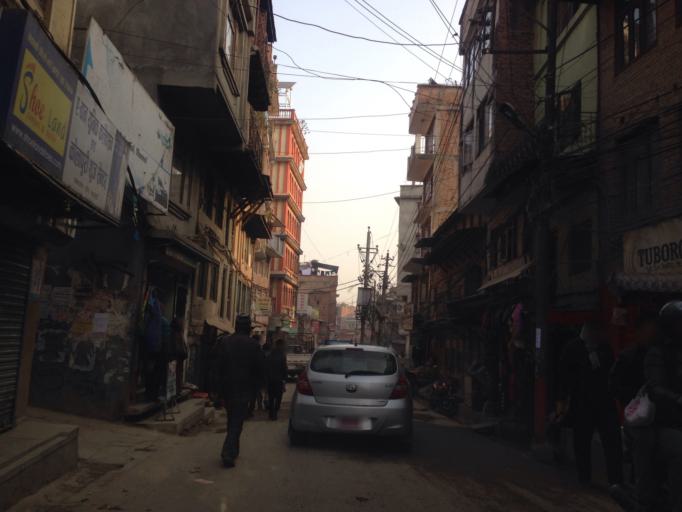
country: NP
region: Central Region
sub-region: Bagmati Zone
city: Kathmandu
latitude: 27.7171
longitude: 85.3089
